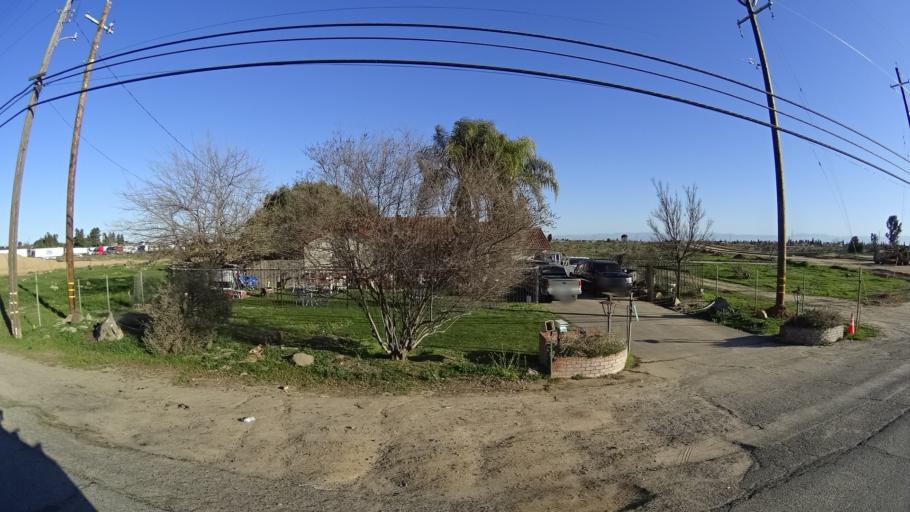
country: US
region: California
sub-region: Fresno County
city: Biola
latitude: 36.8082
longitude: -119.9117
